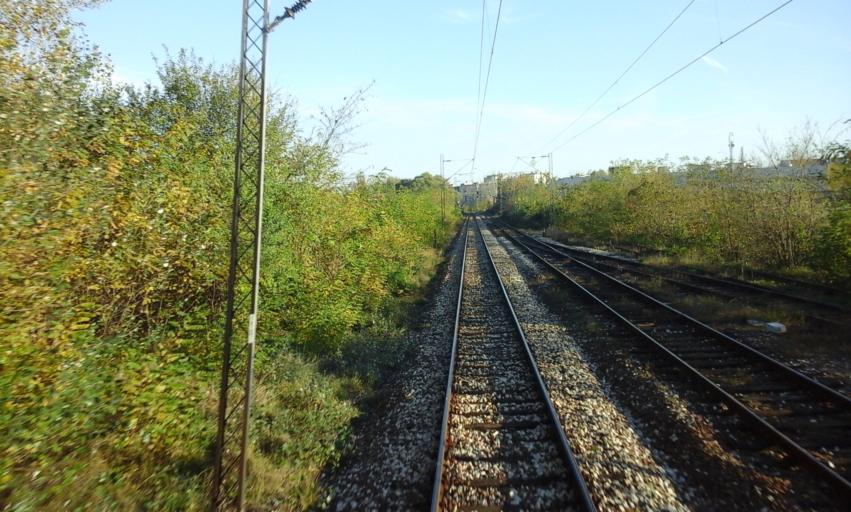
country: RS
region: Autonomna Pokrajina Vojvodina
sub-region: Juznobacki Okrug
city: Novi Sad
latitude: 45.2673
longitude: 19.8160
